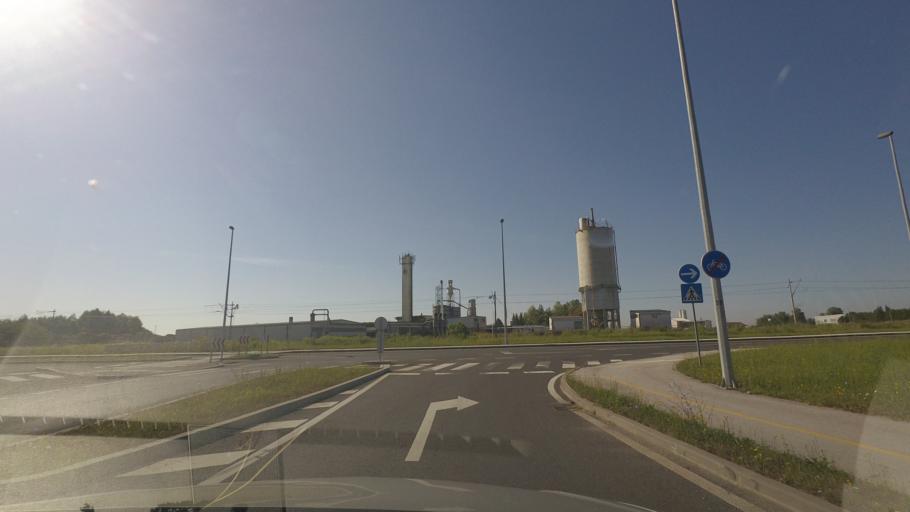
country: HR
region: Zagrebacka
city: Jastrebarsko
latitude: 45.6597
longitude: 15.6553
